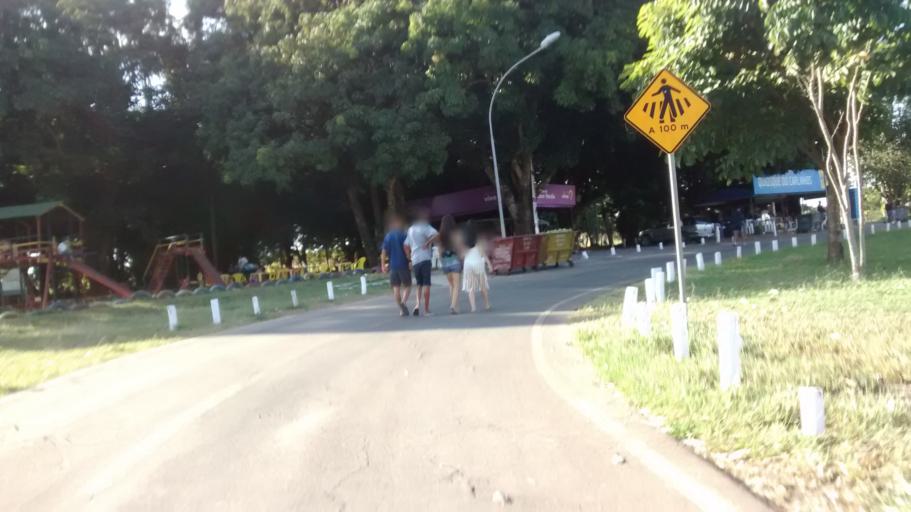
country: BR
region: Federal District
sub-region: Brasilia
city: Brasilia
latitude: -15.8300
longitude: -48.0220
